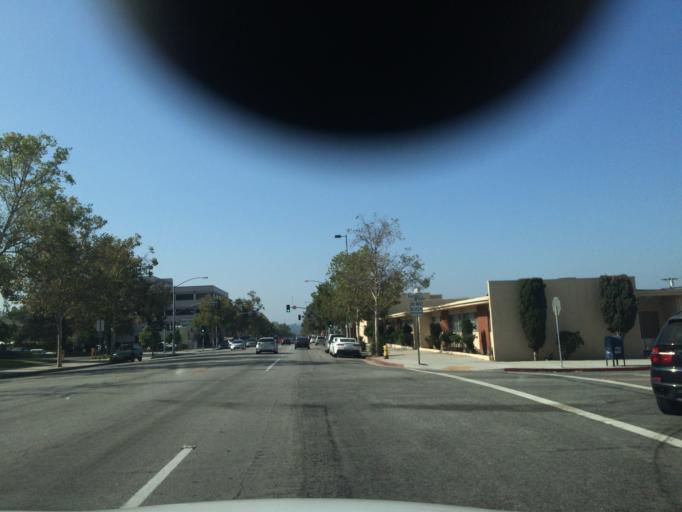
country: US
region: California
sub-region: Los Angeles County
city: Glendale
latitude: 34.1389
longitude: -118.2580
